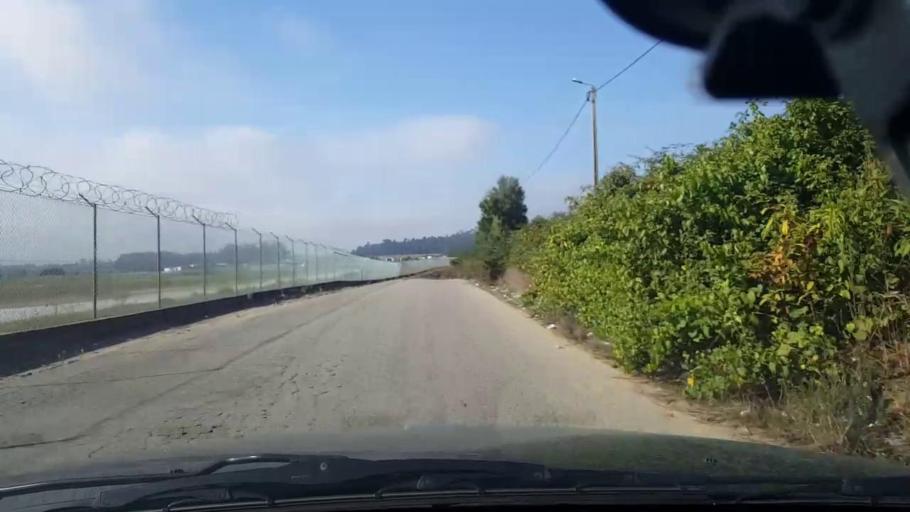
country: PT
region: Porto
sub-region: Matosinhos
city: Lavra
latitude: 41.2642
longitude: -8.6832
